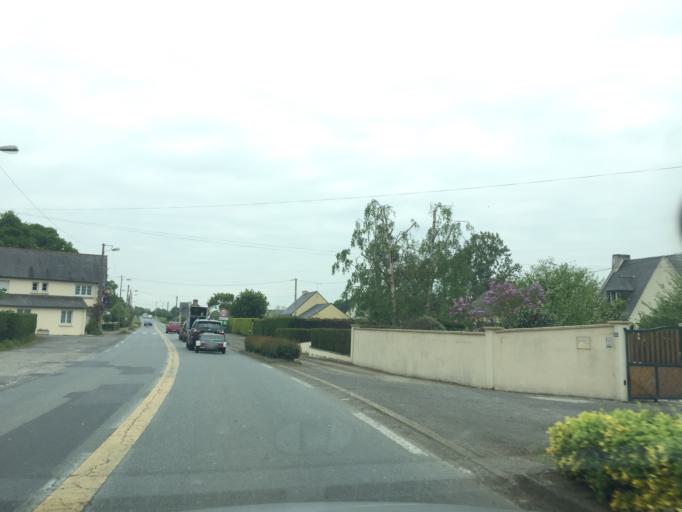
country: FR
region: Brittany
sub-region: Departement des Cotes-d'Armor
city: Lamballe
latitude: 48.5024
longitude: -2.4637
